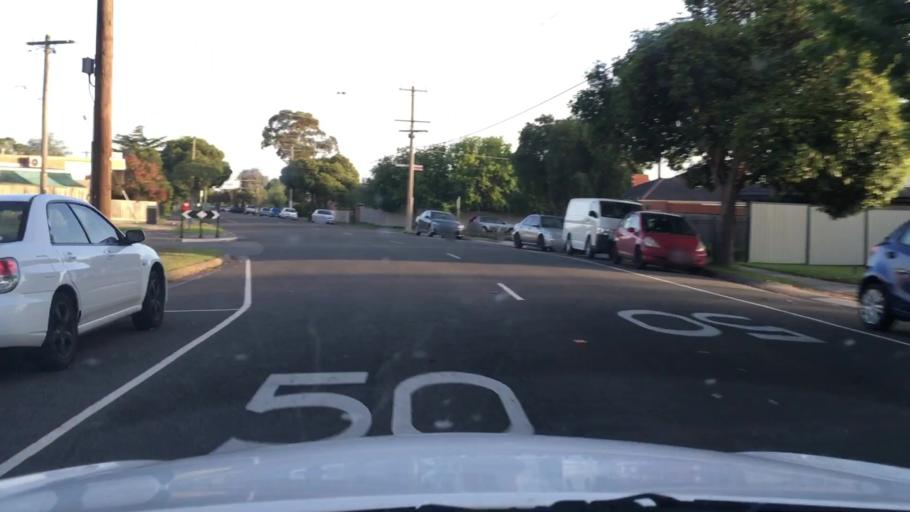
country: AU
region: Victoria
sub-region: Greater Dandenong
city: Noble Park
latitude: -37.9588
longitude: 145.1732
